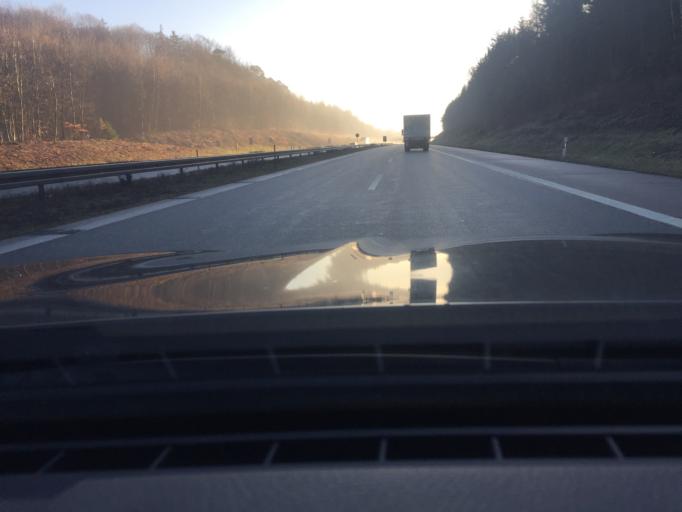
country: DE
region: Bavaria
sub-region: Regierungsbezirk Unterfranken
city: Schondra
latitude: 50.2333
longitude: 9.8843
